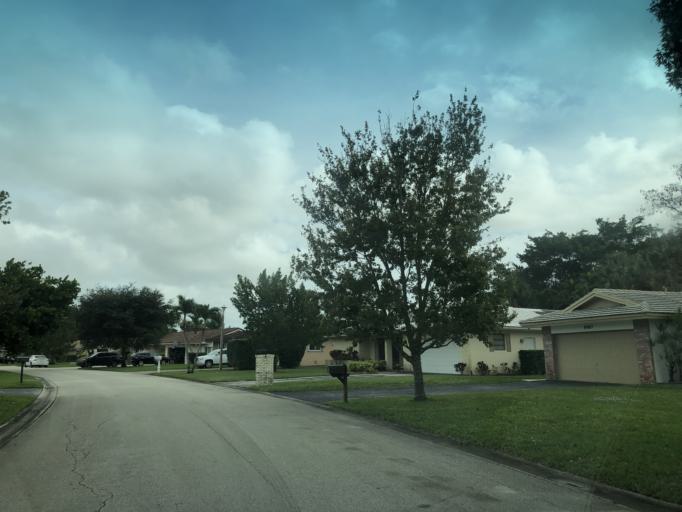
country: US
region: Florida
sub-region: Broward County
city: Margate
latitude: 26.2484
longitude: -80.2399
